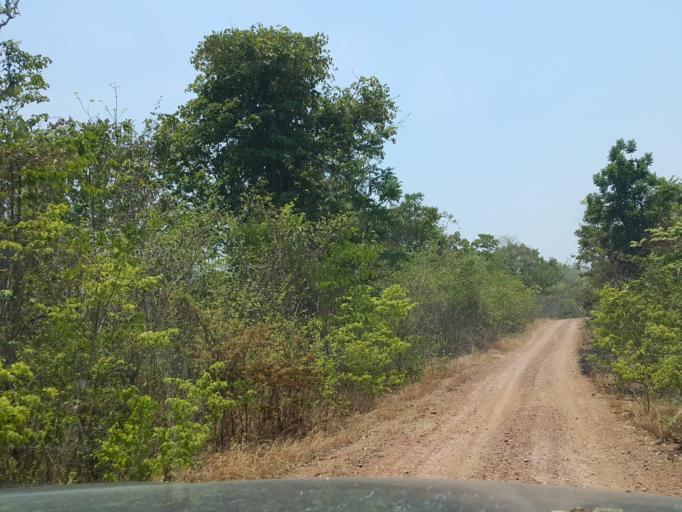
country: TH
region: Lampang
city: Thoen
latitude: 17.6393
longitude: 99.2762
